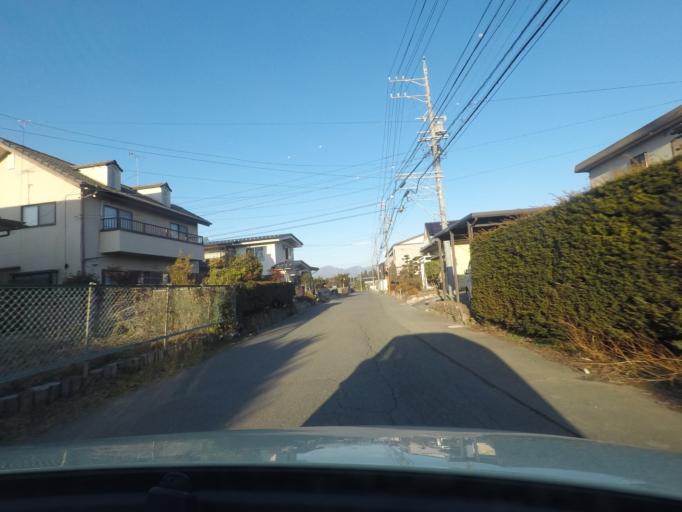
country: JP
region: Nagano
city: Matsumoto
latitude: 36.2107
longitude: 137.8852
